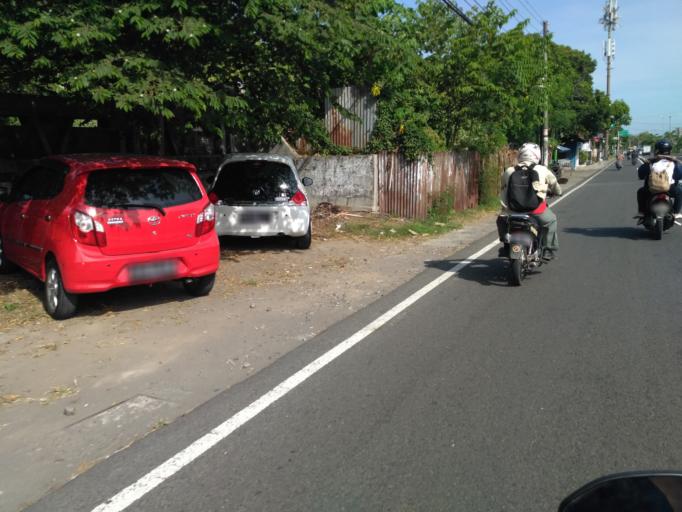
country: ID
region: Daerah Istimewa Yogyakarta
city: Depok
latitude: -7.7790
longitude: 110.4303
